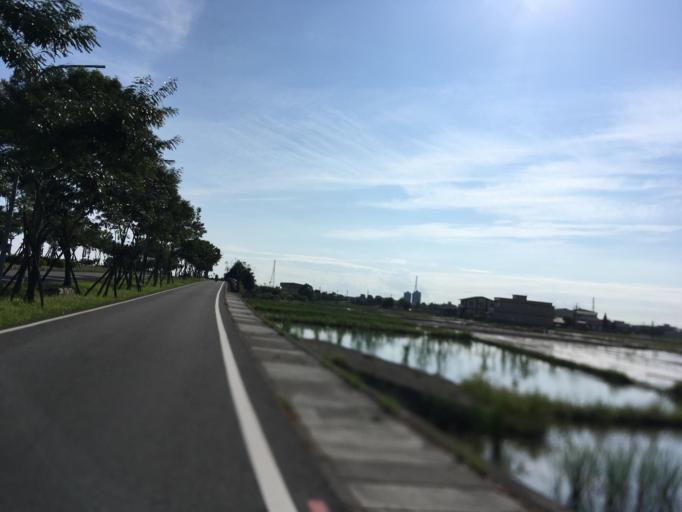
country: TW
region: Taiwan
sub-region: Yilan
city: Yilan
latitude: 24.6777
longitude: 121.7807
